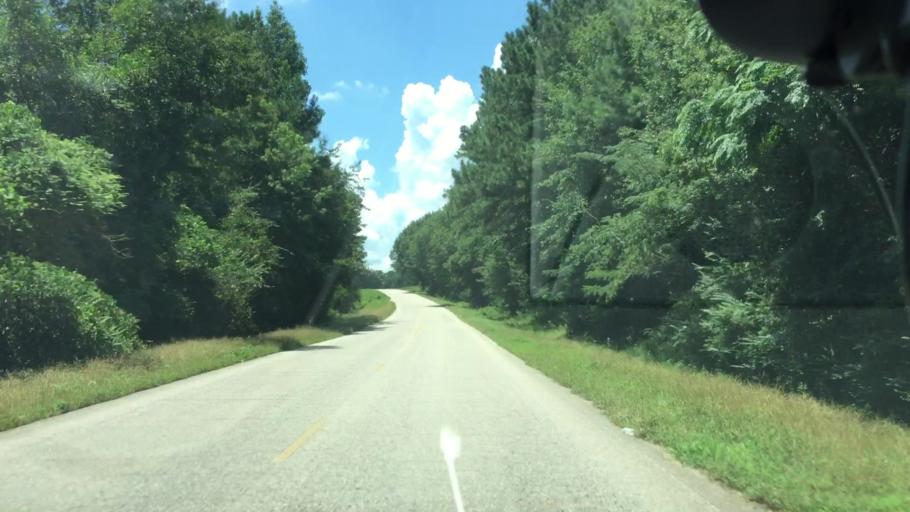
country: US
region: Alabama
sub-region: Pike County
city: Troy
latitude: 31.7466
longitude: -85.9666
